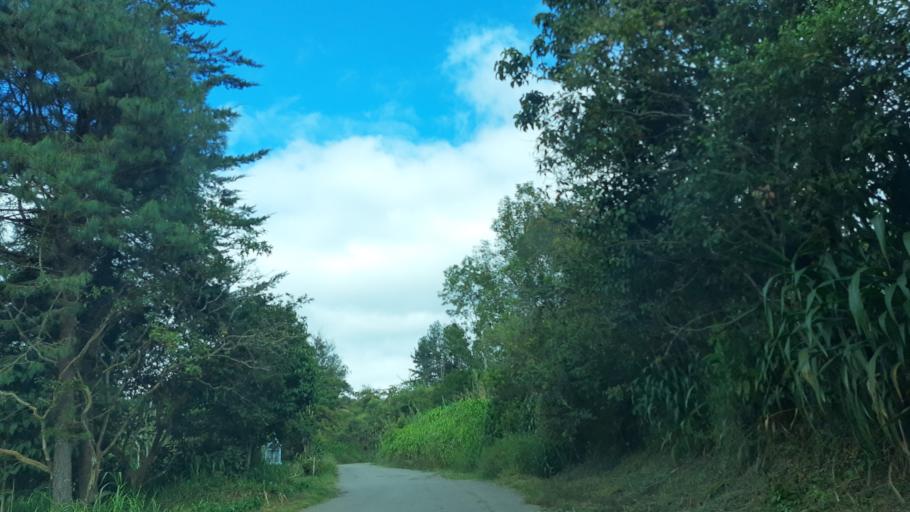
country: CO
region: Cundinamarca
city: Tenza
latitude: 5.0586
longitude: -73.4187
